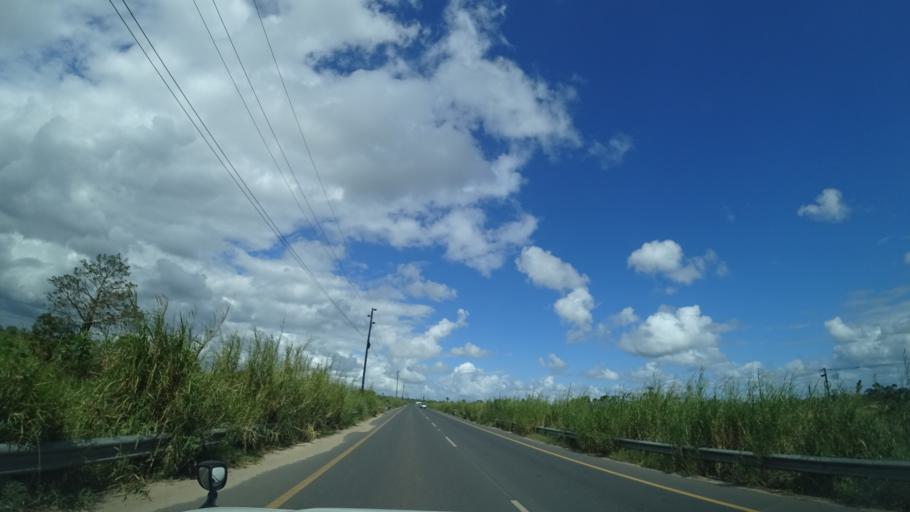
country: MZ
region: Sofala
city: Dondo
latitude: -19.5208
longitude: 34.6221
